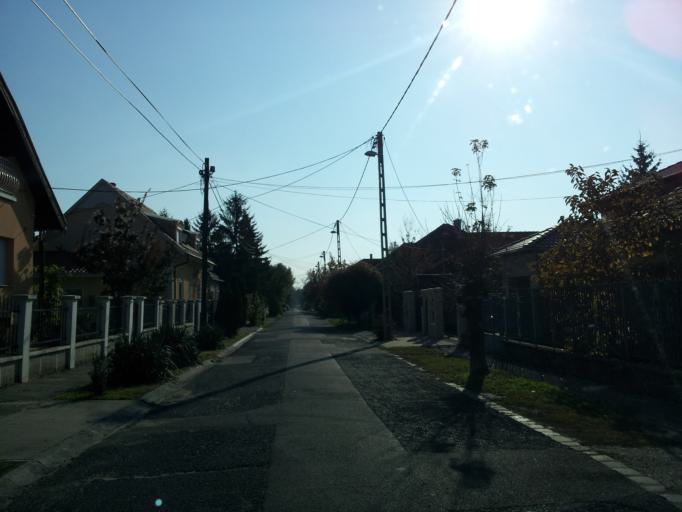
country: HU
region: Budapest
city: Budapest XVIII. keruelet
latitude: 47.4618
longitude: 19.1865
